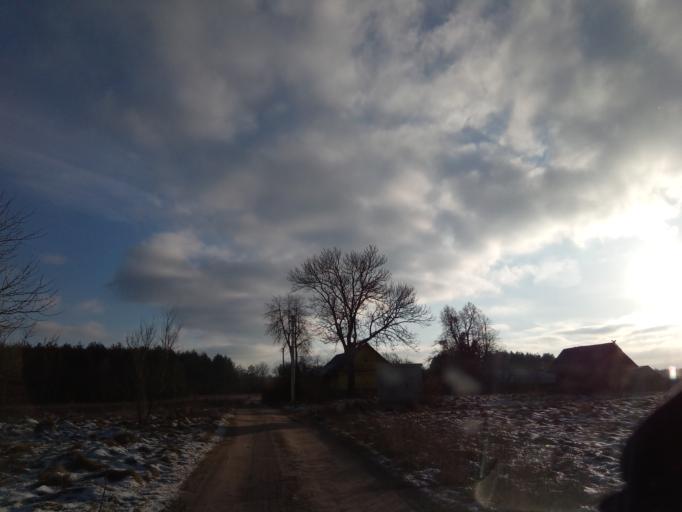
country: LT
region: Alytaus apskritis
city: Druskininkai
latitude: 53.9775
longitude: 24.2422
